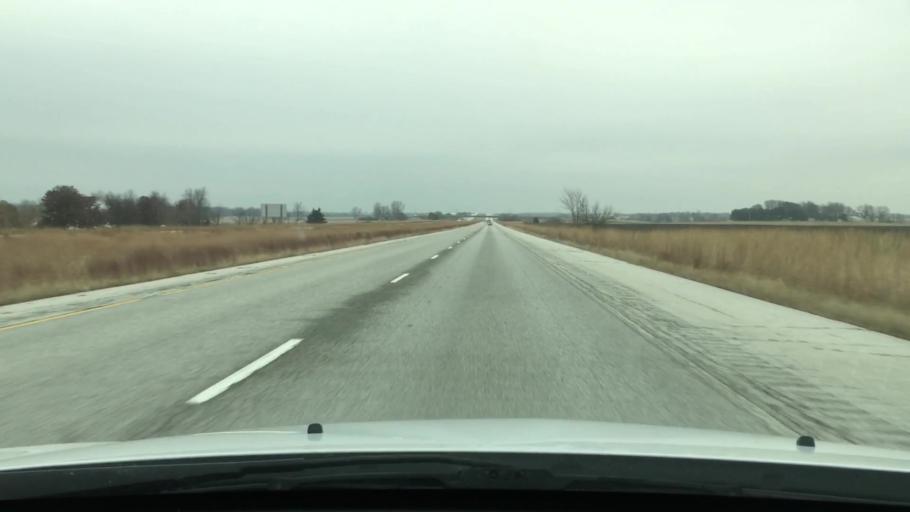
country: US
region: Illinois
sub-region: Morgan County
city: South Jacksonville
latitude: 39.6932
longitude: -90.1975
